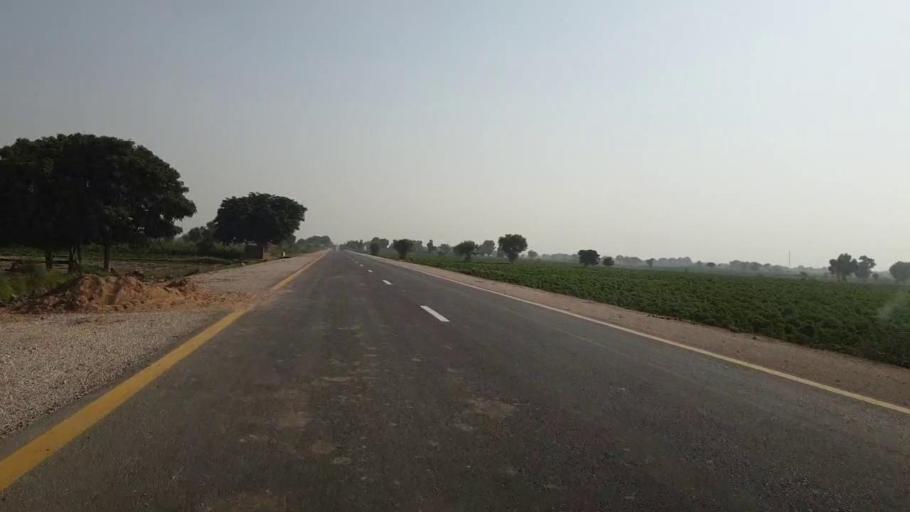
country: PK
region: Sindh
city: Bhan
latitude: 26.5417
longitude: 67.7875
